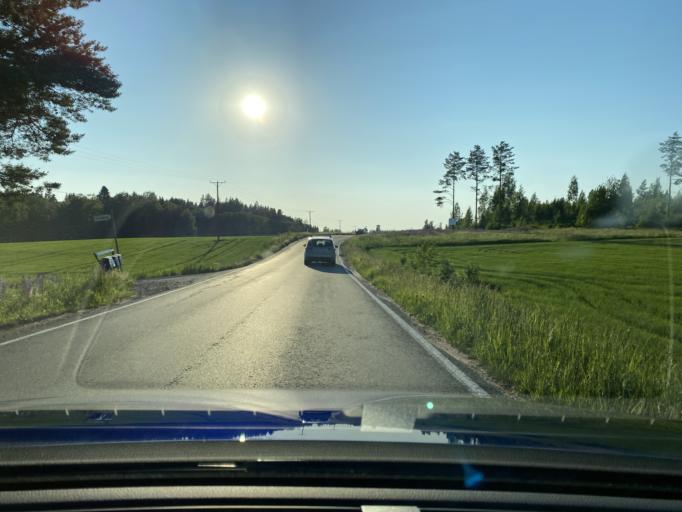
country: FI
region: Haeme
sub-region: Haemeenlinna
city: Tervakoski
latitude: 60.7296
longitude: 24.6758
